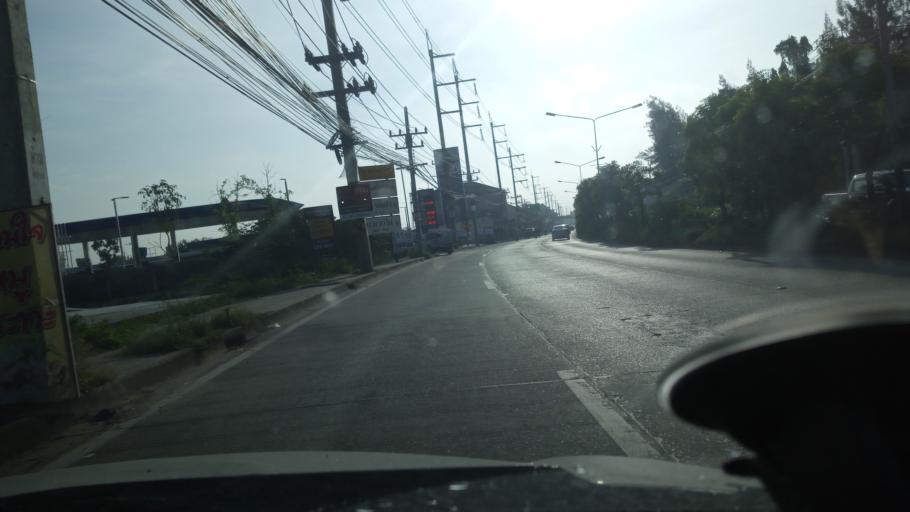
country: TH
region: Chon Buri
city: Phan Thong
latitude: 13.4143
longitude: 101.0623
